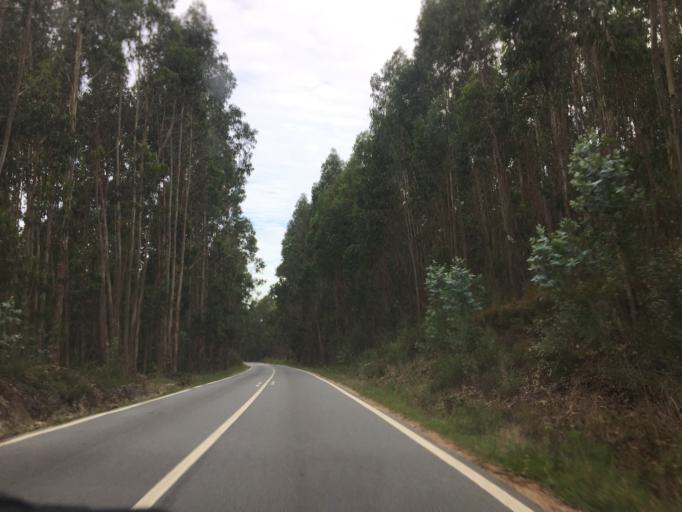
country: PT
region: Aveiro
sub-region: Agueda
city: Aguada de Cima
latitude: 40.4979
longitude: -8.3558
